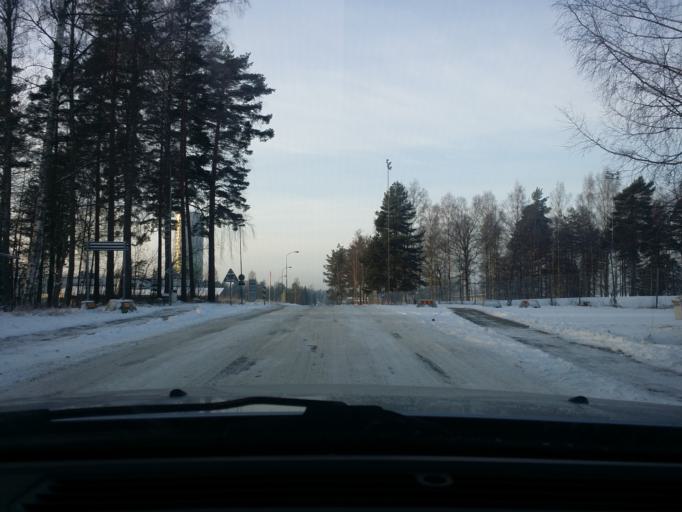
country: SE
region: OErebro
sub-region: Lindesbergs Kommun
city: Lindesberg
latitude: 59.5999
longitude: 15.2072
